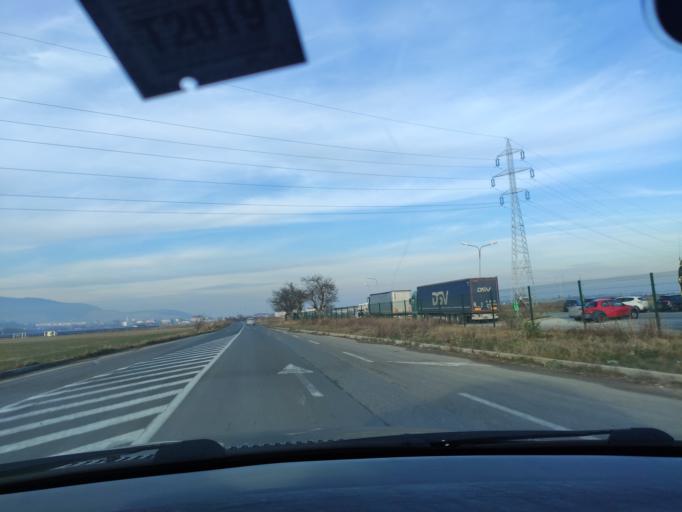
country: RO
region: Brasov
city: Codlea
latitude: 45.6766
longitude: 25.4442
